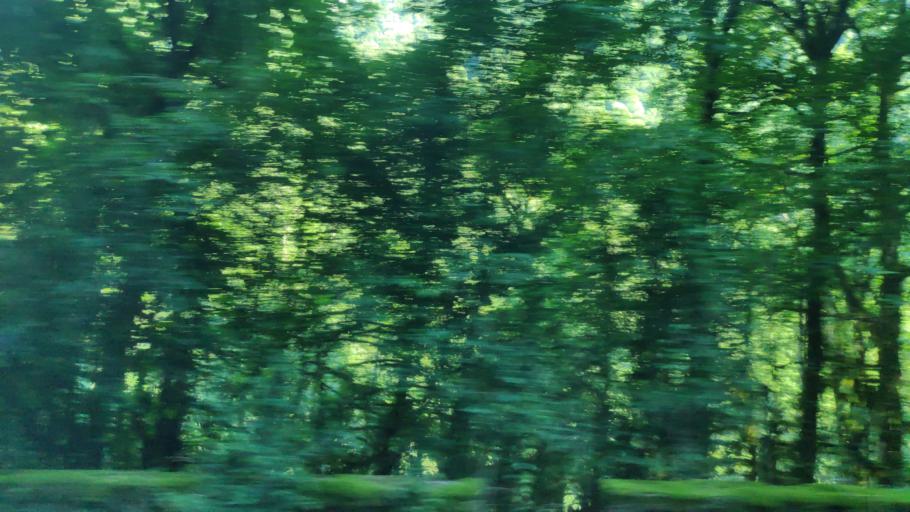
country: GE
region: Abkhazia
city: Gagra
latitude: 43.3556
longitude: 40.4229
